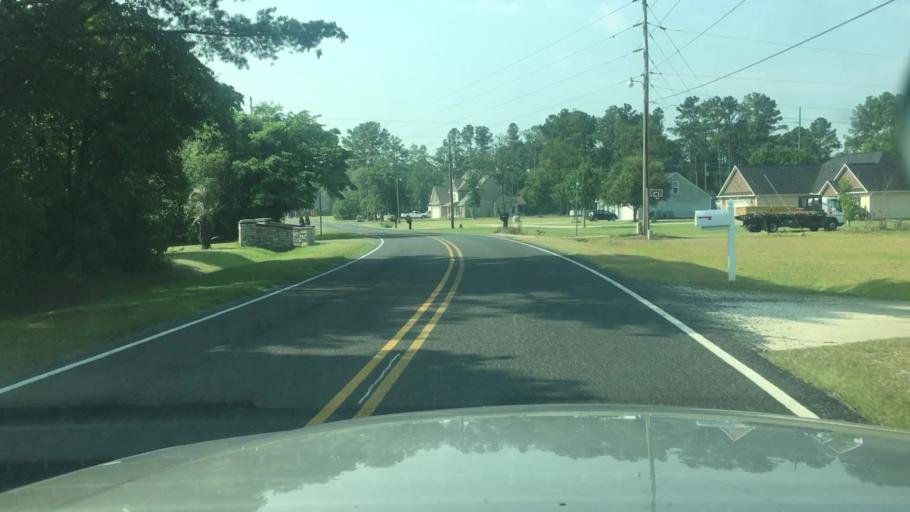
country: US
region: North Carolina
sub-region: Cumberland County
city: Hope Mills
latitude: 34.9046
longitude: -78.8720
